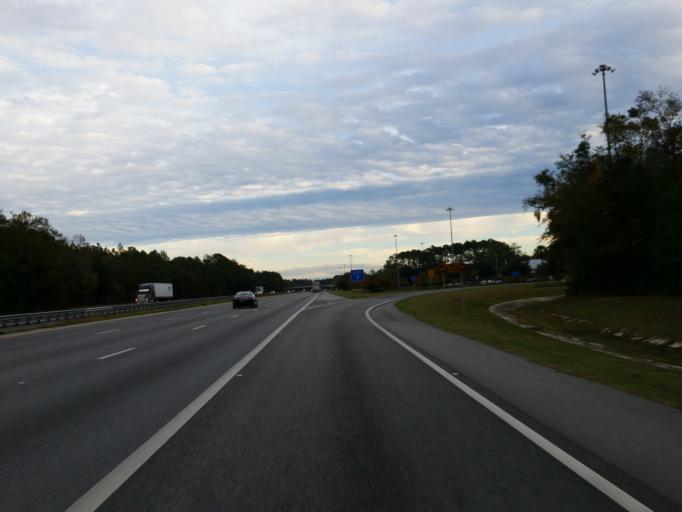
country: US
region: Georgia
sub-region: Echols County
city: Statenville
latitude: 30.6152
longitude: -83.1499
